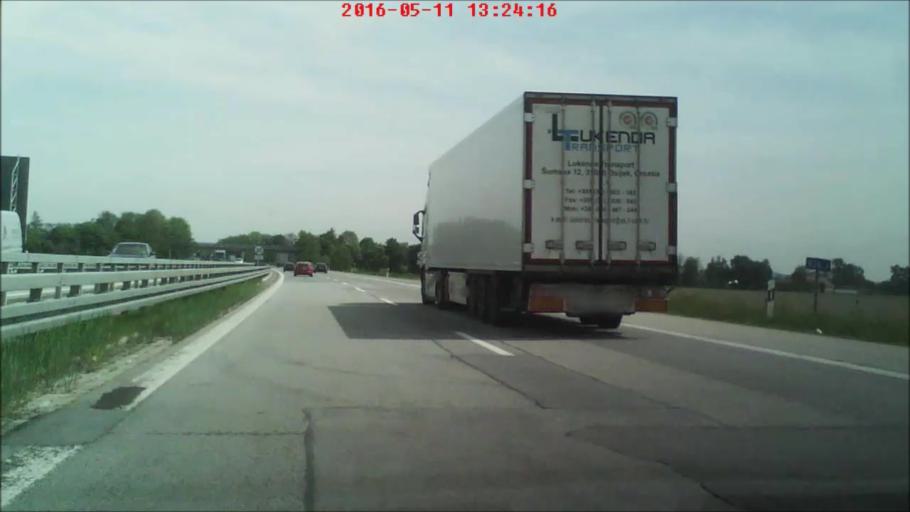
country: AT
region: Upper Austria
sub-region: Politischer Bezirk Scharding
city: Scharding
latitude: 48.4299
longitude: 13.3815
